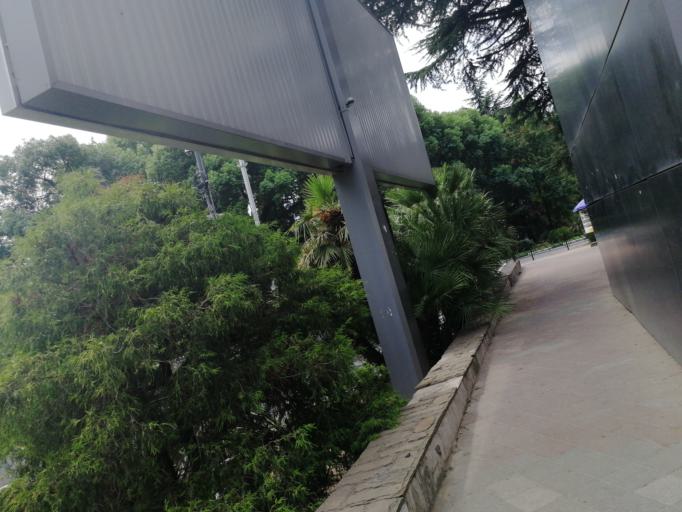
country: RU
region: Krasnodarskiy
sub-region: Sochi City
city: Sochi
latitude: 43.5827
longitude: 39.7222
